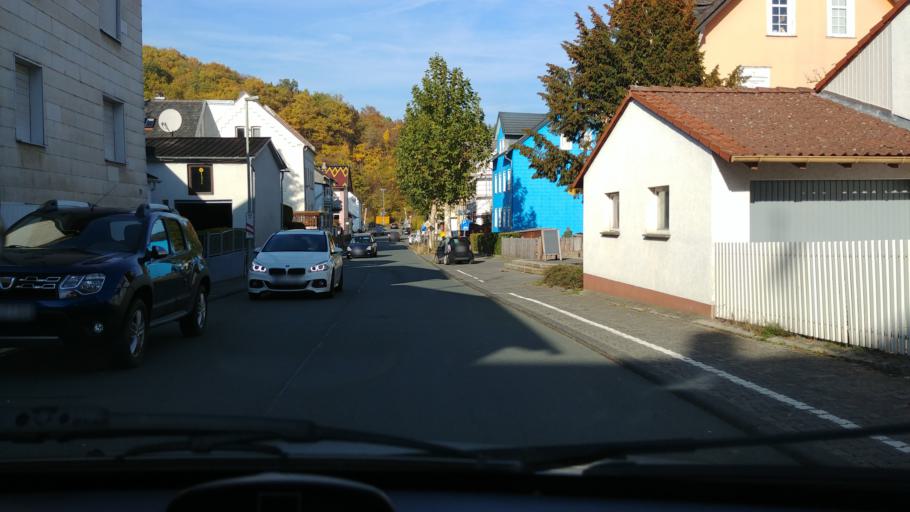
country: DE
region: Hesse
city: Burg Hohenstein
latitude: 50.2320
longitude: 8.0584
